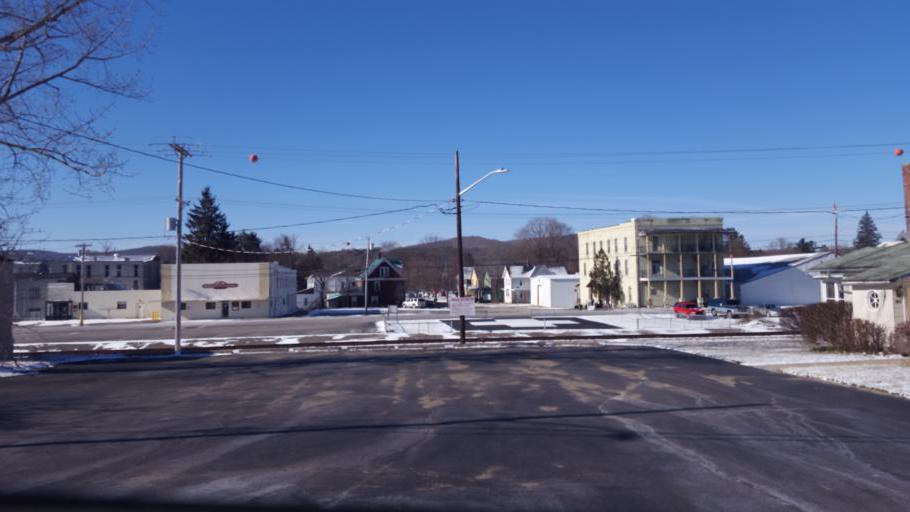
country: US
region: New York
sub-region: Allegany County
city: Wellsville
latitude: 42.1247
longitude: -77.9487
